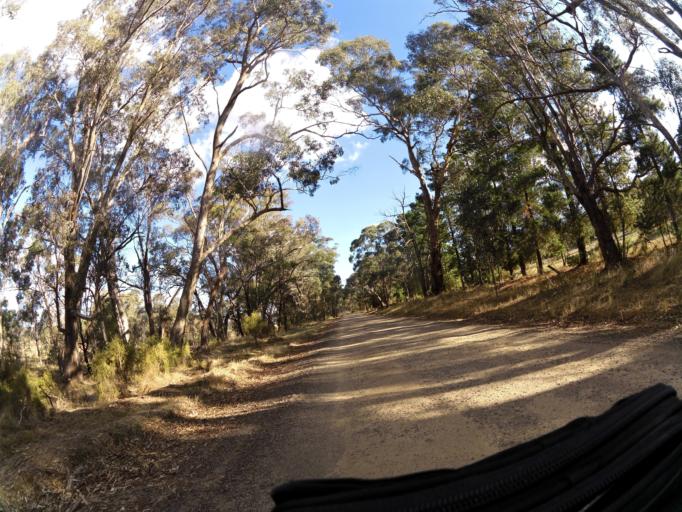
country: AU
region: Victoria
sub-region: Greater Bendigo
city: Kennington
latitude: -37.0126
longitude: 144.8087
